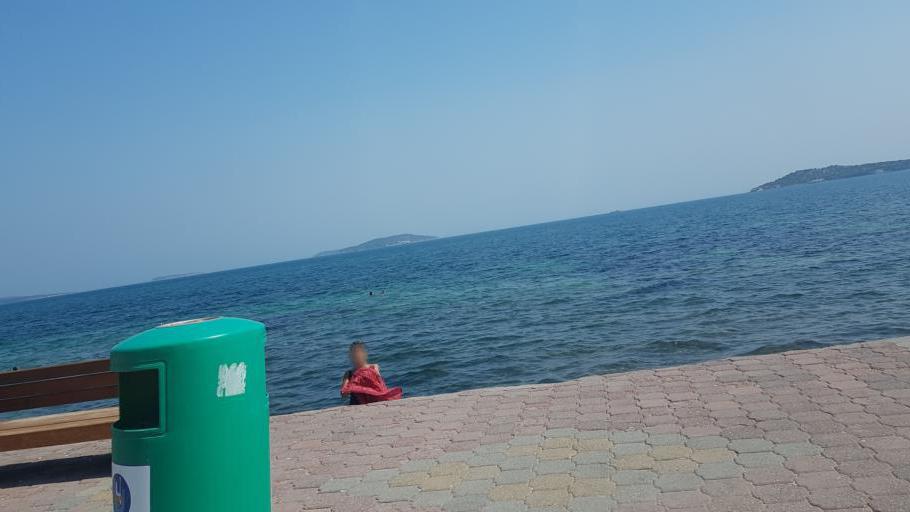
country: TR
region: Izmir
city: Urla
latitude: 38.3674
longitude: 26.7654
